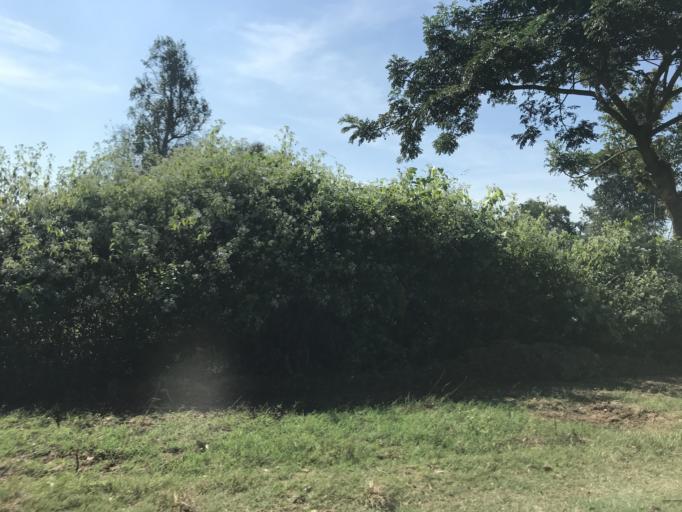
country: IN
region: Karnataka
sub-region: Mysore
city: Heggadadevankote
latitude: 12.0465
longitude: 76.3374
